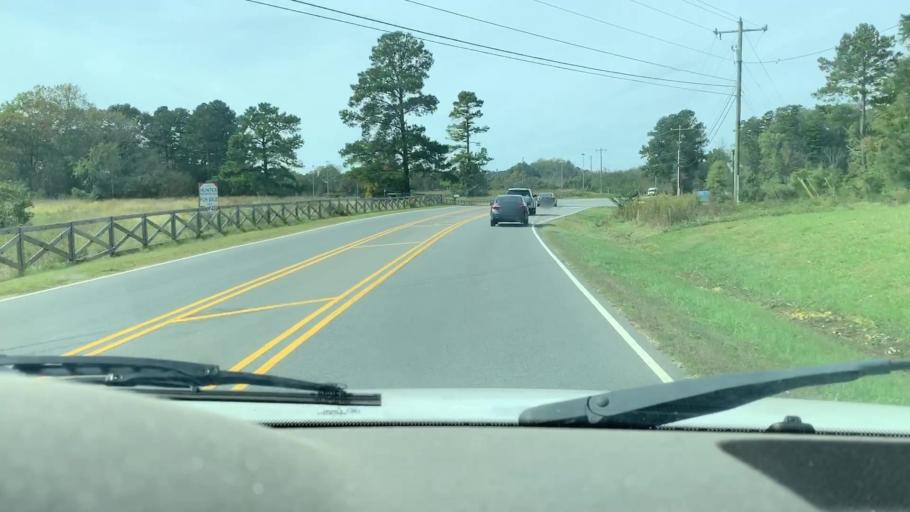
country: US
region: North Carolina
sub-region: Mecklenburg County
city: Huntersville
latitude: 35.4465
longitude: -80.7848
